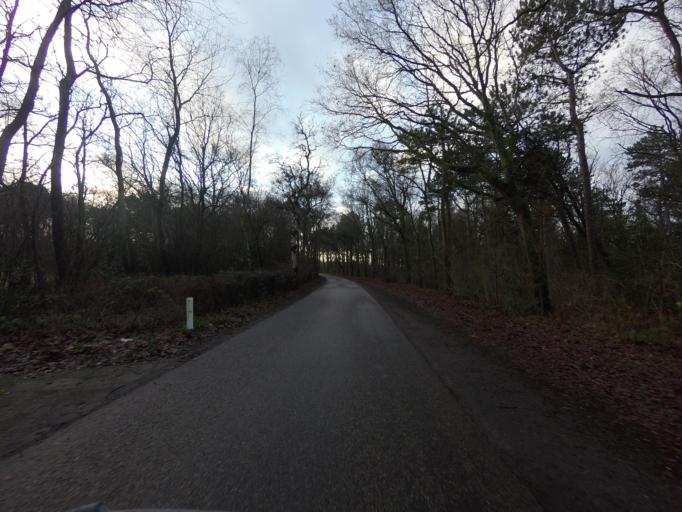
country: NL
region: North Holland
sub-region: Gemeente Texel
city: Den Burg
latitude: 53.0964
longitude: 4.7730
